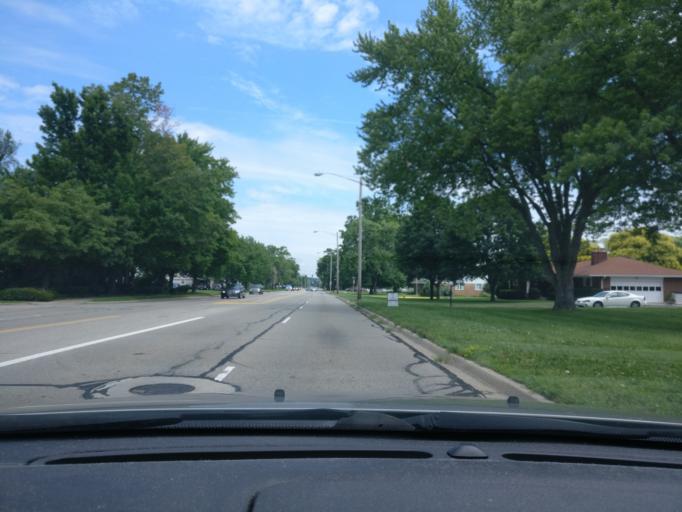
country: US
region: Ohio
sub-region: Montgomery County
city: West Carrollton City
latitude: 39.6633
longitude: -84.2416
